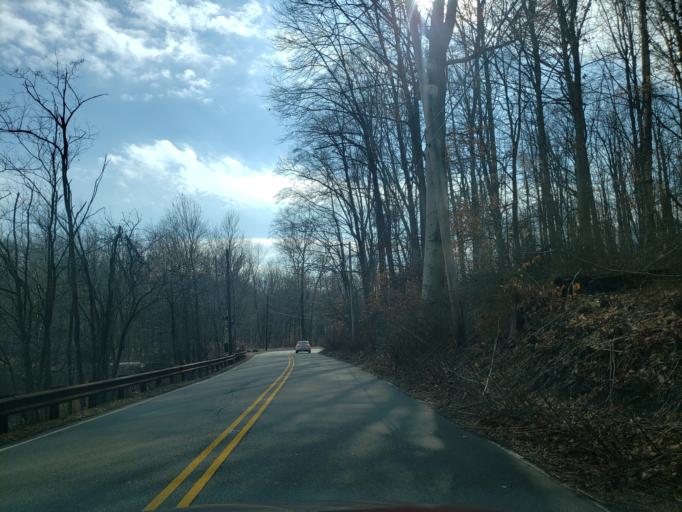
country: US
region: New Jersey
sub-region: Essex County
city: Short Hills
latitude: 40.7318
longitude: -74.3077
